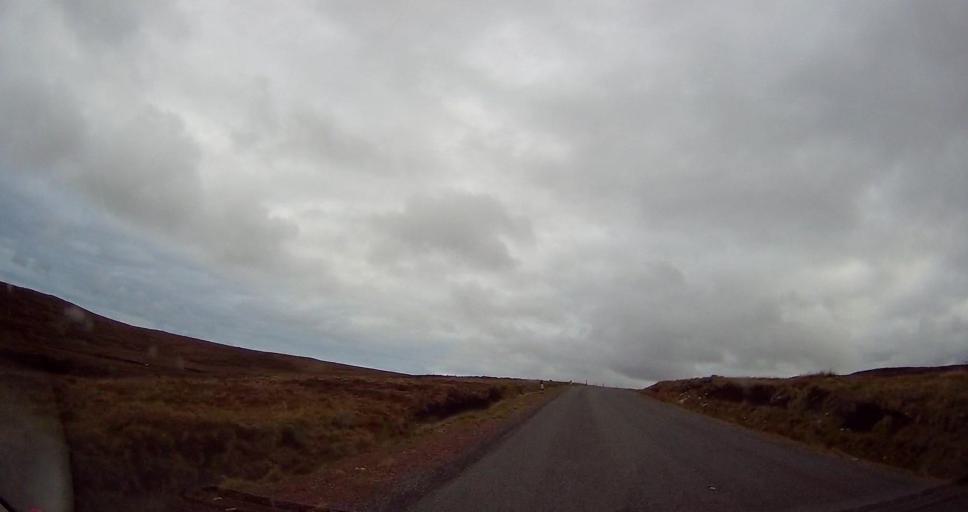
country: GB
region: Scotland
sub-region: Shetland Islands
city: Shetland
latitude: 60.6234
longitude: -1.0736
